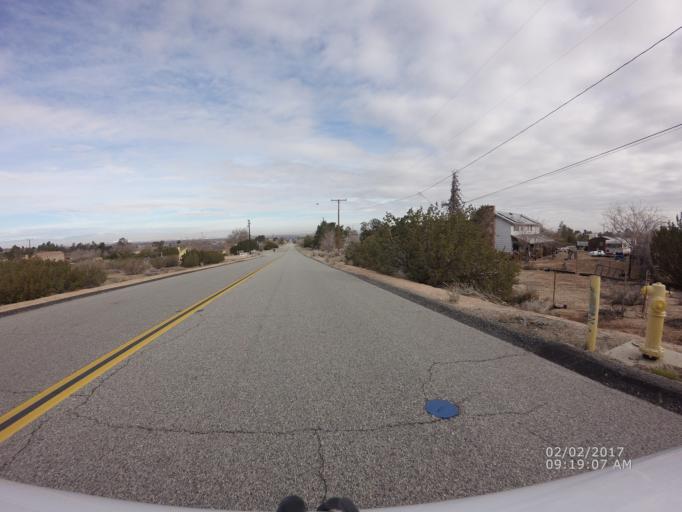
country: US
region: California
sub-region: Los Angeles County
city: Vincent
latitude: 34.5347
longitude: -118.0584
